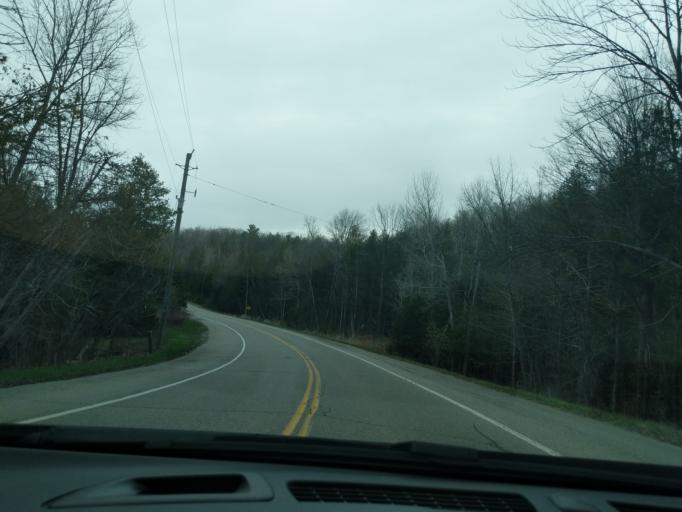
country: CA
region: Ontario
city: Orangeville
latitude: 43.9985
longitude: -80.0016
